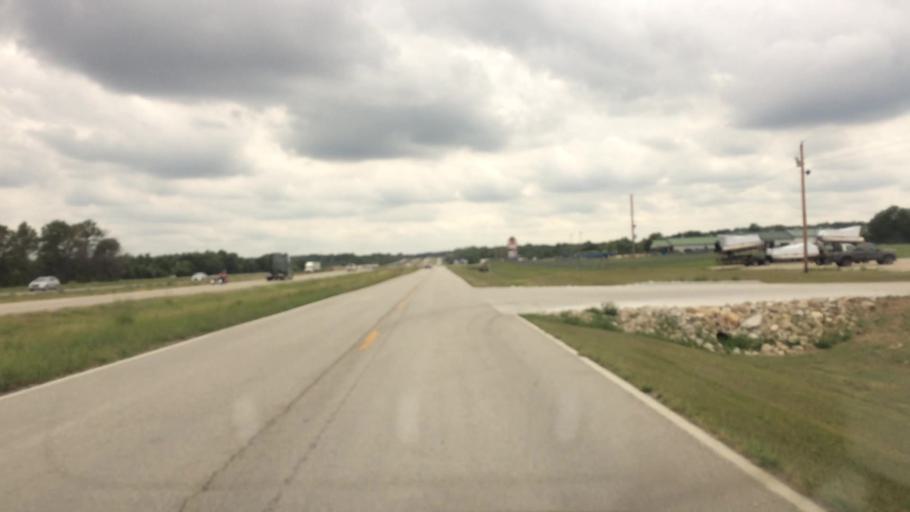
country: US
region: Missouri
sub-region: Greene County
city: Strafford
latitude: 37.2945
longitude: -93.0239
